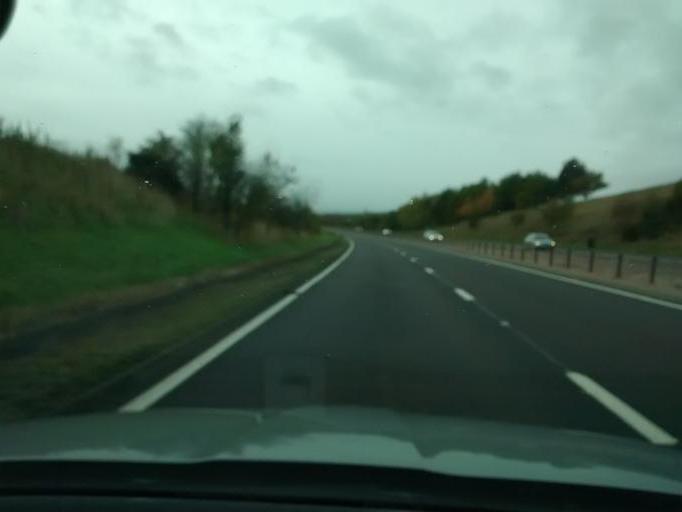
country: GB
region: Scotland
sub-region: Perth and Kinross
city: Methven
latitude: 56.3423
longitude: -3.5994
